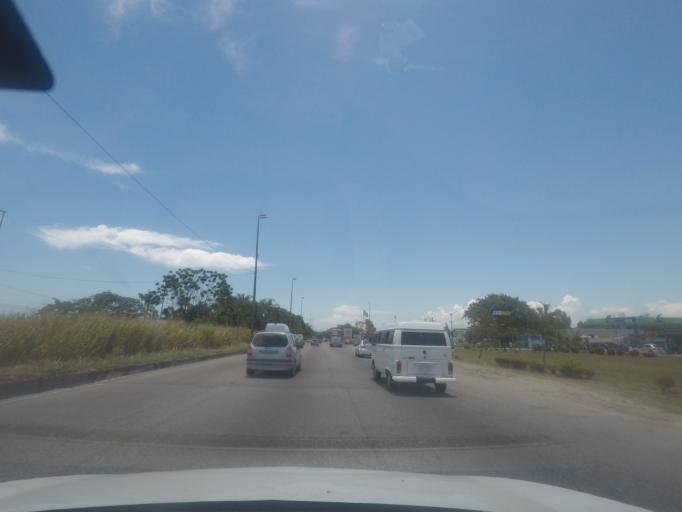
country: BR
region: Rio de Janeiro
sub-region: Itaguai
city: Itaguai
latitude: -22.8923
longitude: -43.6715
